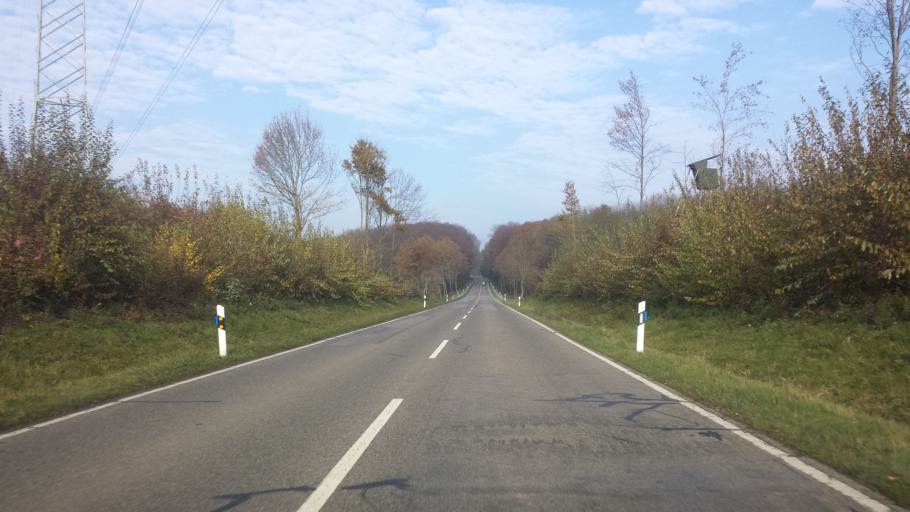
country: DE
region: Baden-Wuerttemberg
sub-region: Karlsruhe Region
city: Huffenhardt
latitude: 49.3088
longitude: 9.0778
